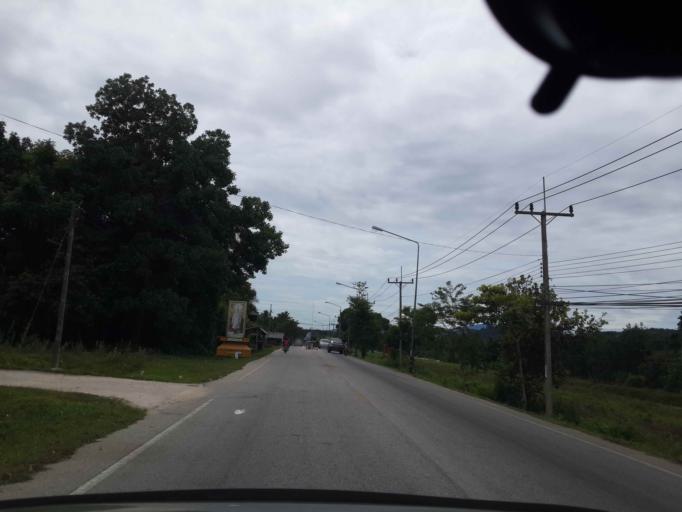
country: TH
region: Narathiwat
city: Yi-ngo
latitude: 6.3399
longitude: 101.6319
